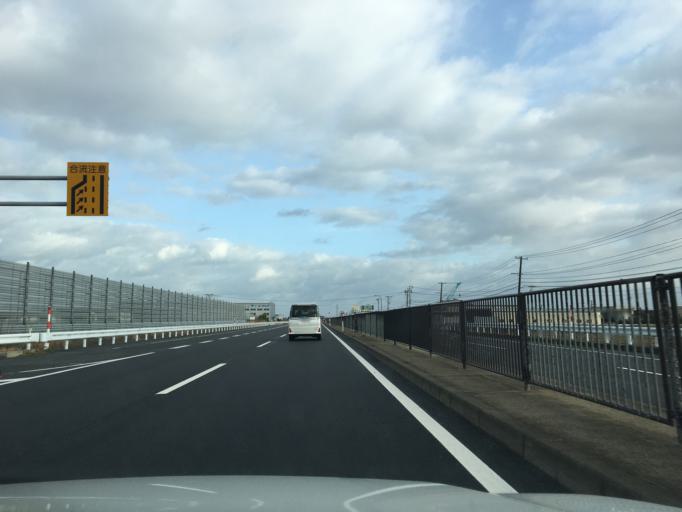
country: JP
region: Yamagata
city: Sakata
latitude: 38.8740
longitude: 139.8404
